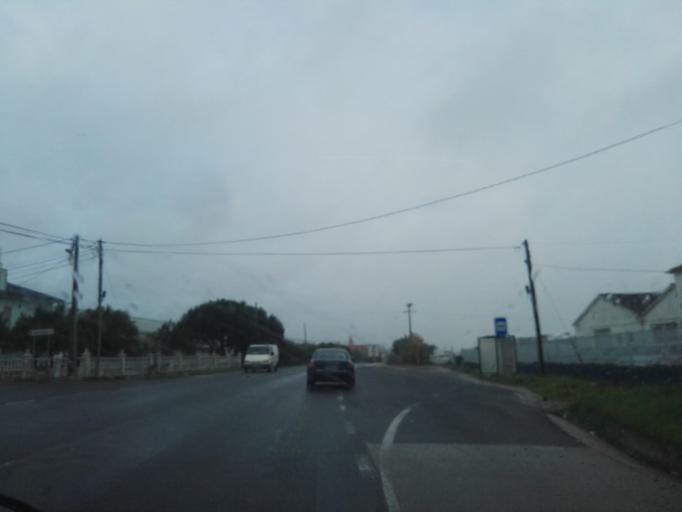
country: PT
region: Lisbon
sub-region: Alenquer
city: Carregado
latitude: 39.0401
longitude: -8.9305
